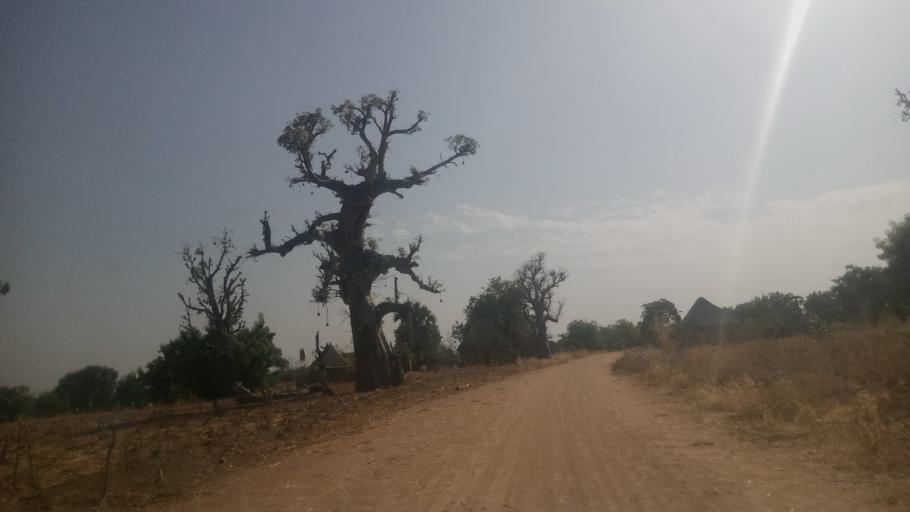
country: NG
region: Adamawa
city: Mayo Belwa
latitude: 9.0746
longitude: 12.0350
